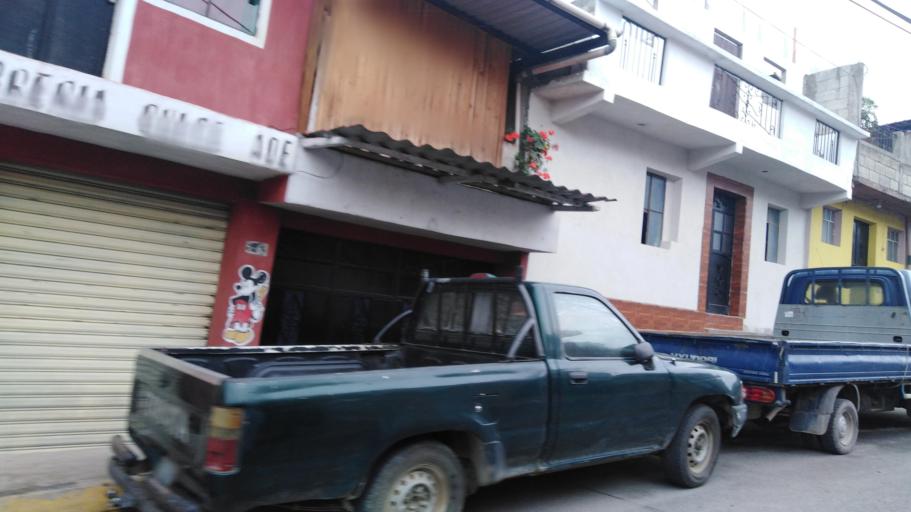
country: GT
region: Quetzaltenango
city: Quetzaltenango
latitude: 14.8510
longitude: -91.5116
